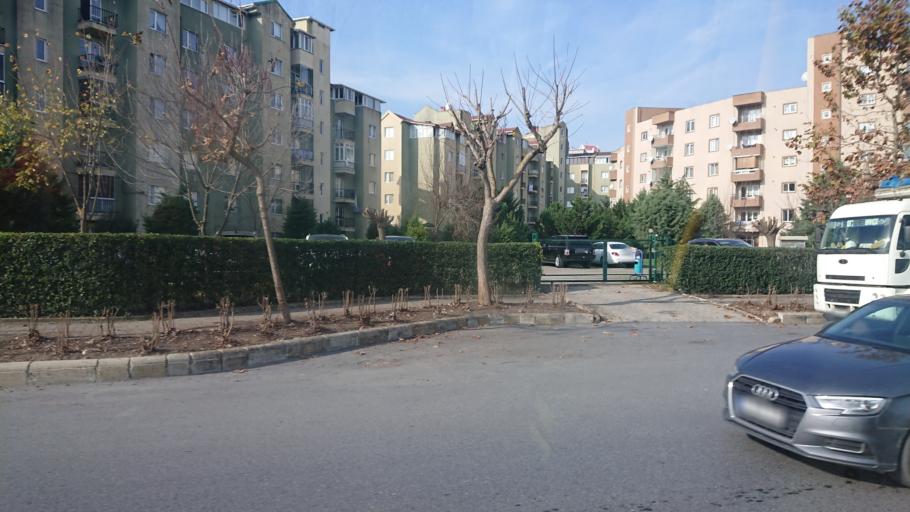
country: TR
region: Istanbul
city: Esenyurt
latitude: 41.0712
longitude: 28.6663
